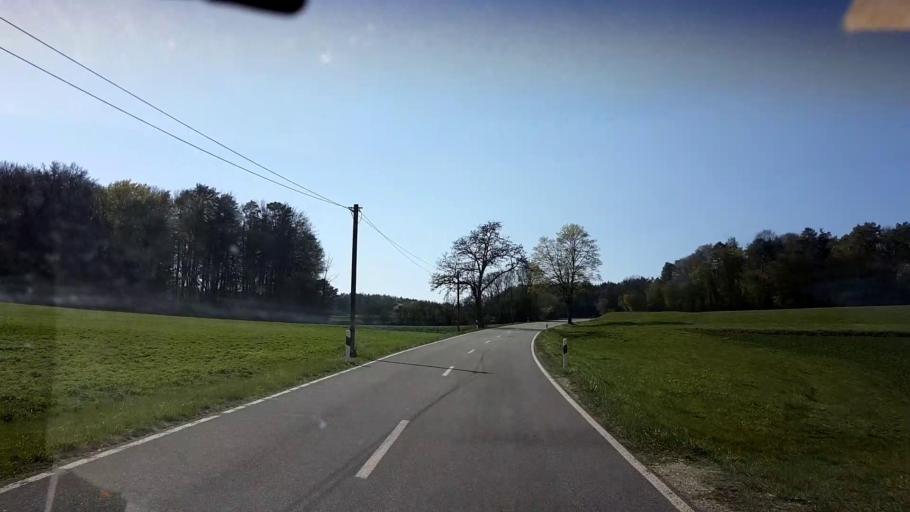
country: DE
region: Bavaria
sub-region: Upper Franconia
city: Pottenstein
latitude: 49.7911
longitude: 11.4173
